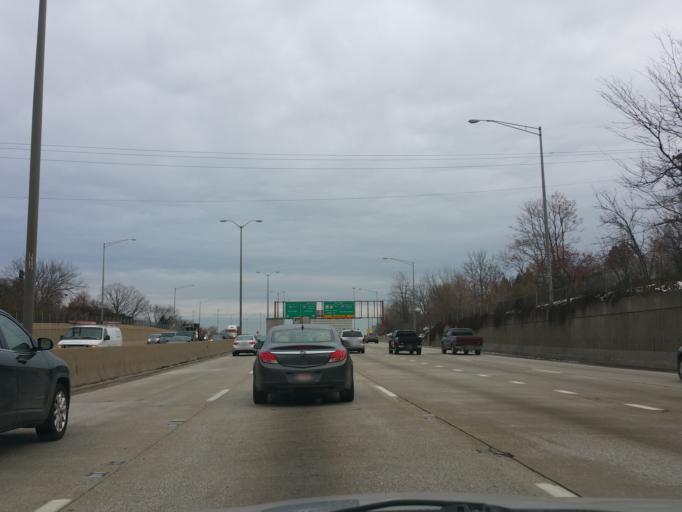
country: US
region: Illinois
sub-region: DuPage County
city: Elmhurst
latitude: 41.9096
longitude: -87.9309
